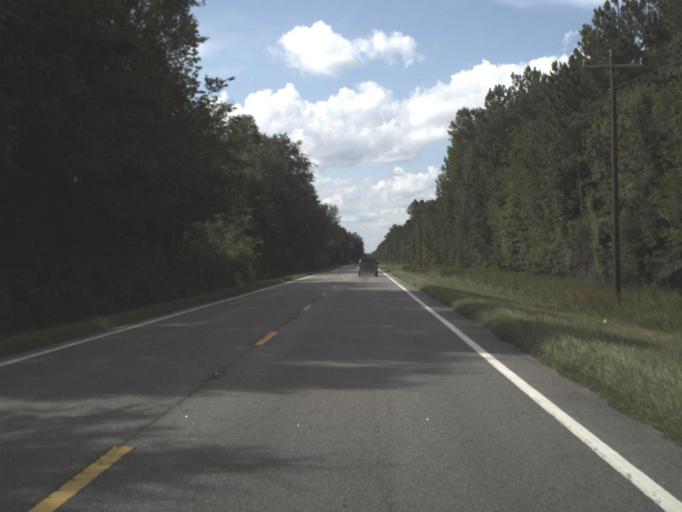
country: US
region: Florida
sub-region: Taylor County
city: Perry
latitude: 30.3136
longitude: -83.6393
